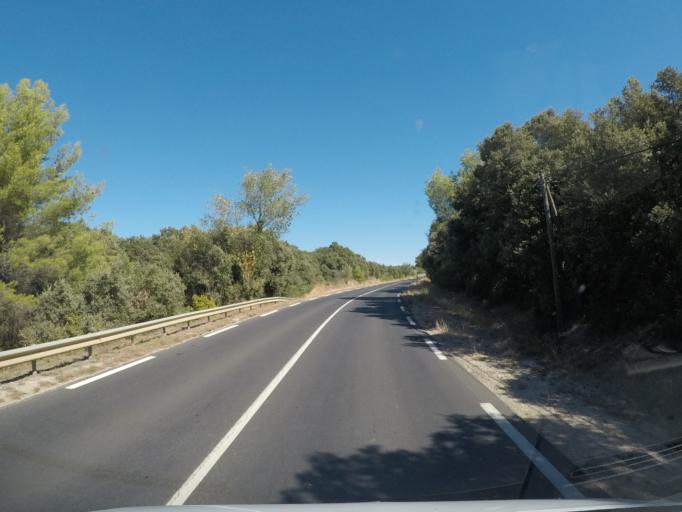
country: FR
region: Languedoc-Roussillon
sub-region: Departement de l'Herault
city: Aniane
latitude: 43.7033
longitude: 3.5951
